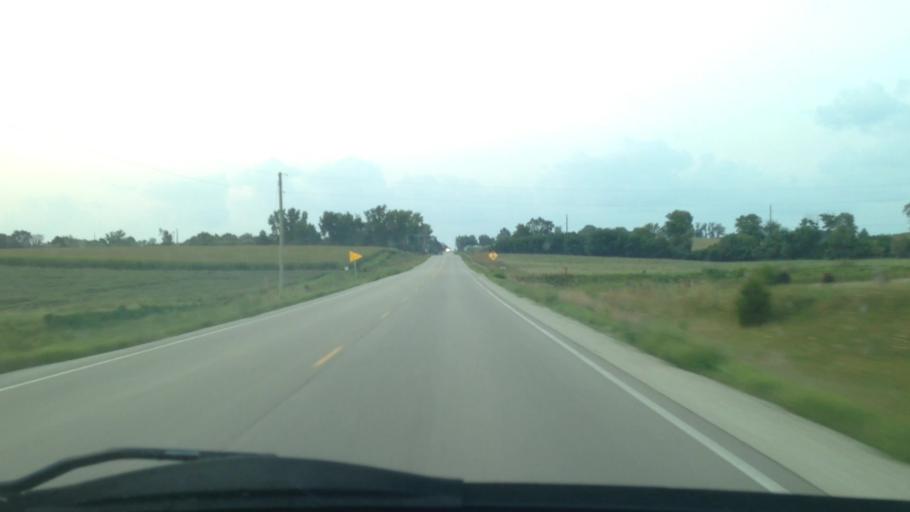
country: US
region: Iowa
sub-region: Benton County
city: Urbana
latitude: 42.2149
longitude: -91.8714
